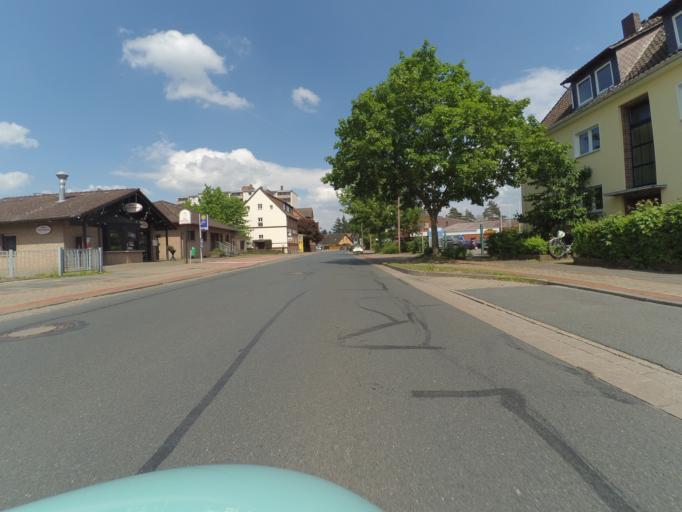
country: DE
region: Lower Saxony
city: Lehrte
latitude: 52.3695
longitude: 9.9719
